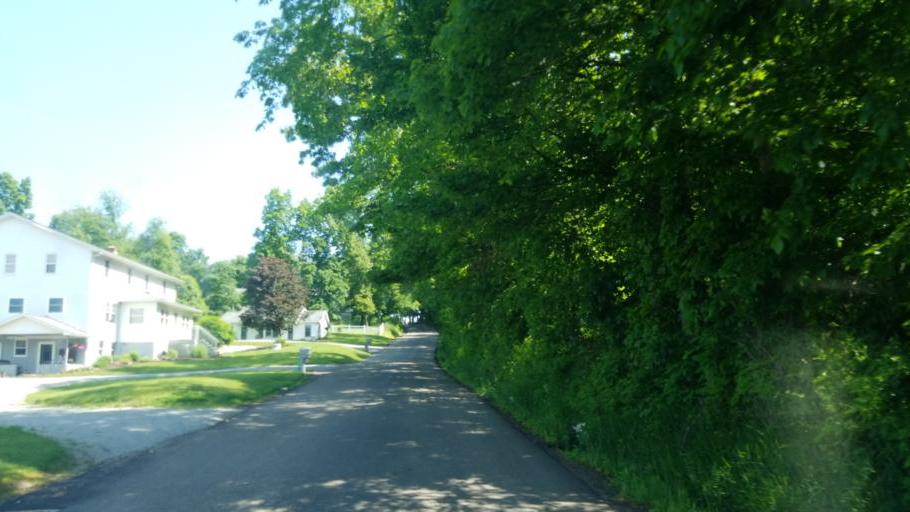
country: US
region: Ohio
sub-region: Holmes County
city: Millersburg
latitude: 40.5281
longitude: -81.7798
